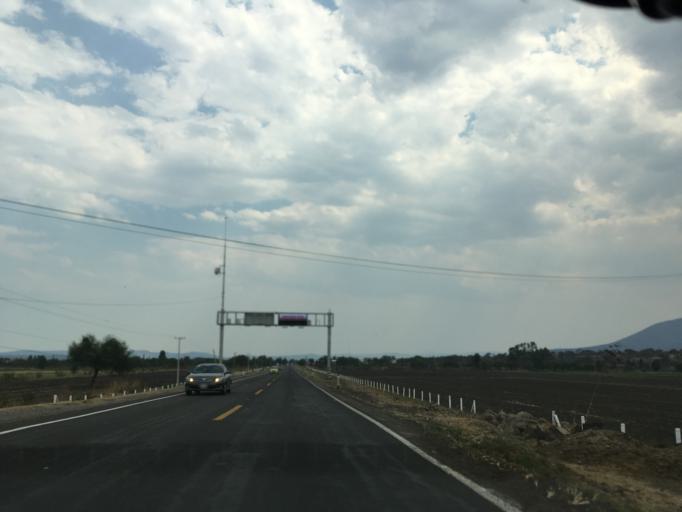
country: MX
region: Michoacan
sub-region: Cuitzeo
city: Cuamio
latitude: 20.0492
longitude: -101.1509
